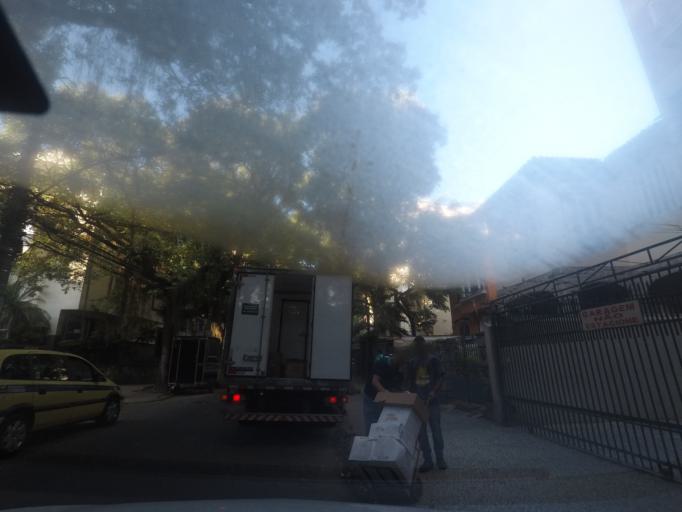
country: BR
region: Rio de Janeiro
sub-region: Rio De Janeiro
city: Rio de Janeiro
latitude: -22.9578
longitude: -43.1851
